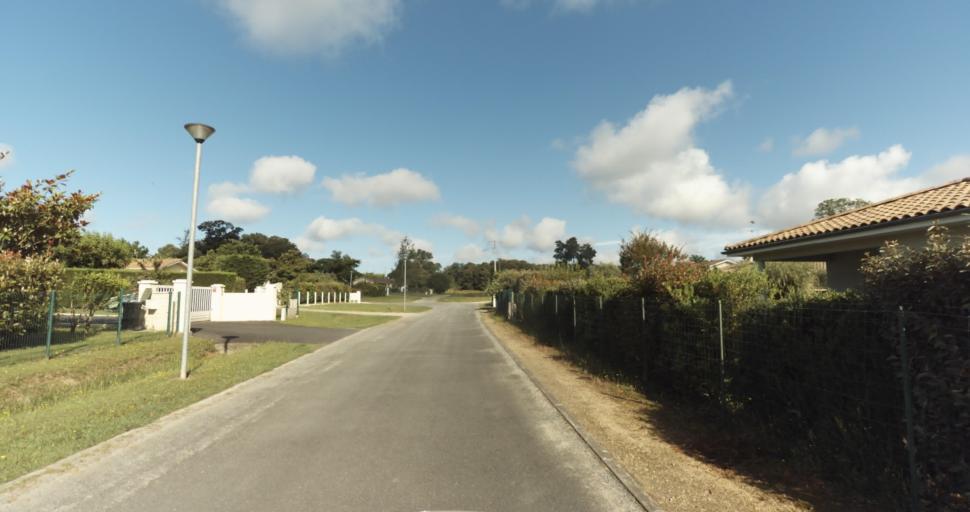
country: FR
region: Aquitaine
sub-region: Departement de la Gironde
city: Bazas
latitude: 44.4356
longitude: -0.2425
